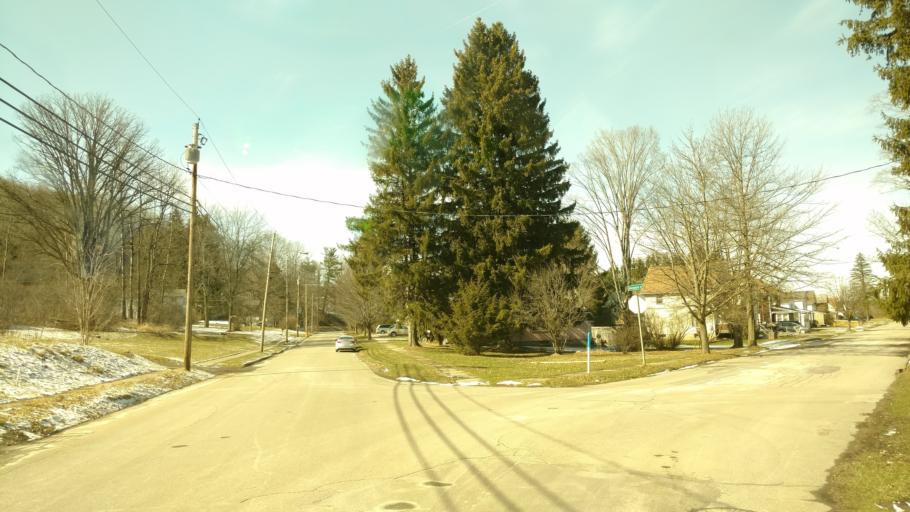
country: US
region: New York
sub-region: Allegany County
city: Wellsville
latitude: 42.1204
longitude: -77.9585
